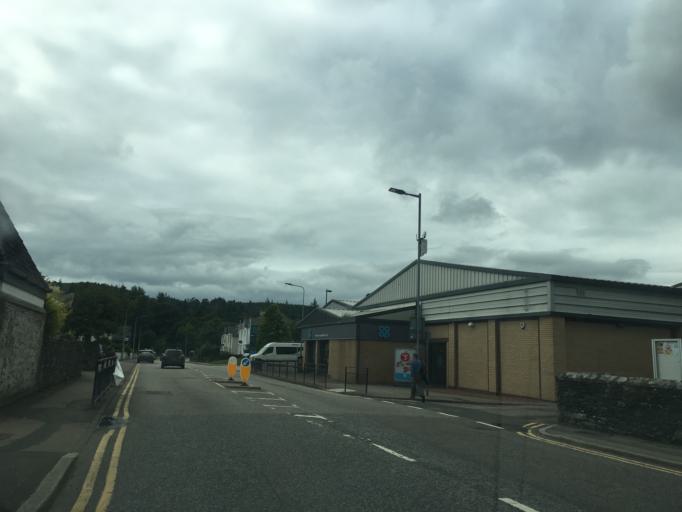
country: GB
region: Scotland
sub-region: Argyll and Bute
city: Lochgilphead
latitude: 56.0391
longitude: -5.4327
